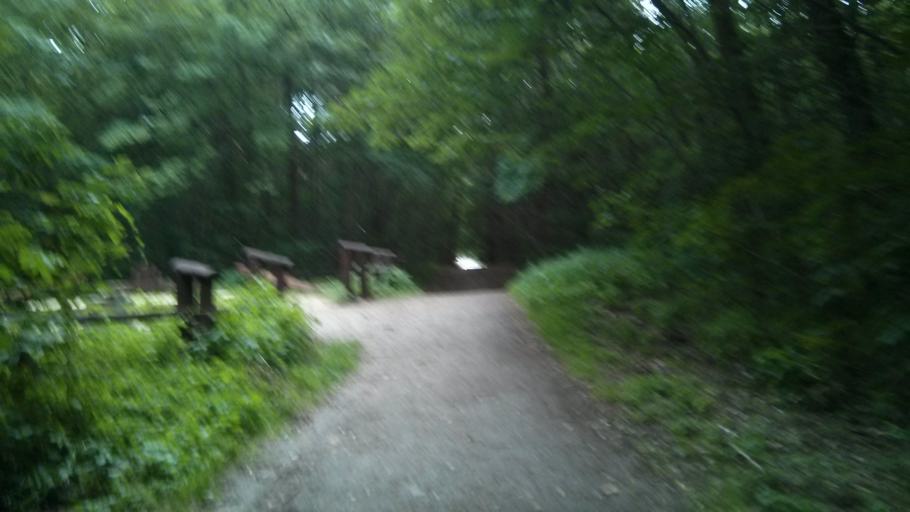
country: PL
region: Masovian Voivodeship
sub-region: Warszawa
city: Wola
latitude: 52.2509
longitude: 20.9528
